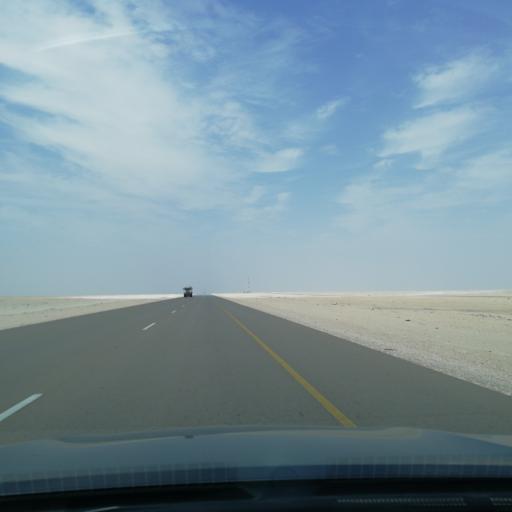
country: OM
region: Al Wusta
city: Hayma'
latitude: 20.2276
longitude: 56.5639
